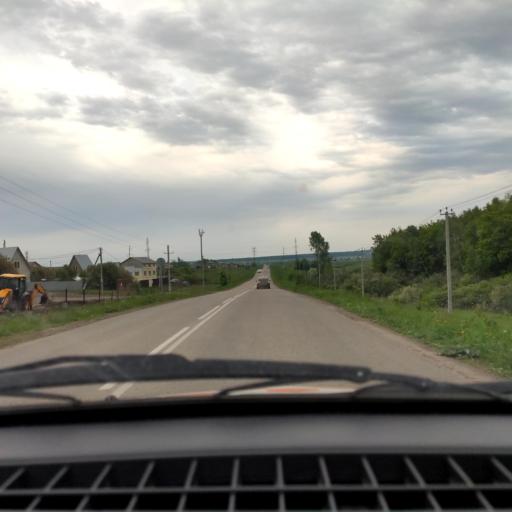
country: RU
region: Bashkortostan
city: Avdon
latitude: 54.5757
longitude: 55.7535
